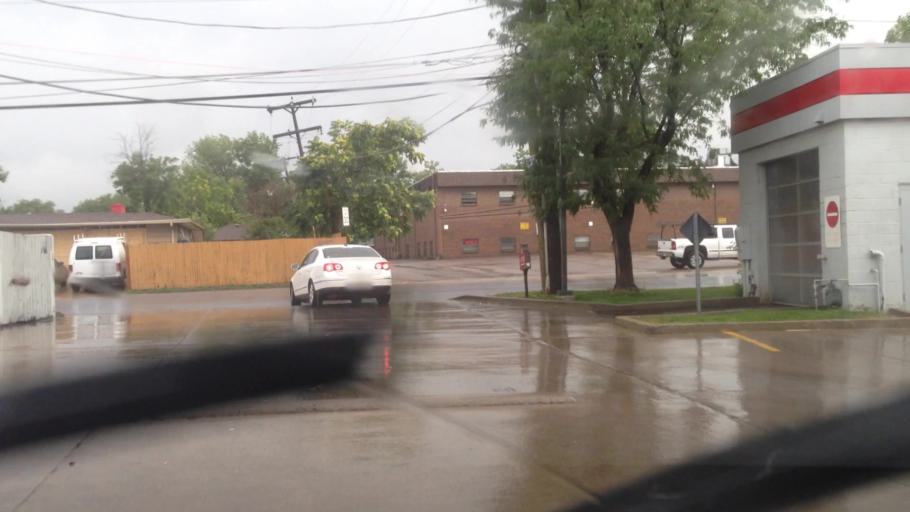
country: US
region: Colorado
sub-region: Jefferson County
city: Edgewater
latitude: 39.7243
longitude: -105.0526
